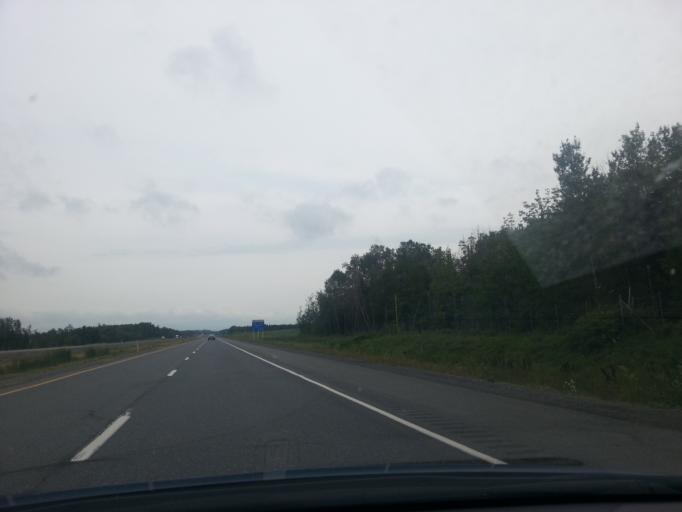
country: CA
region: New Brunswick
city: Florenceville-Bristol
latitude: 46.3165
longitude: -67.5907
